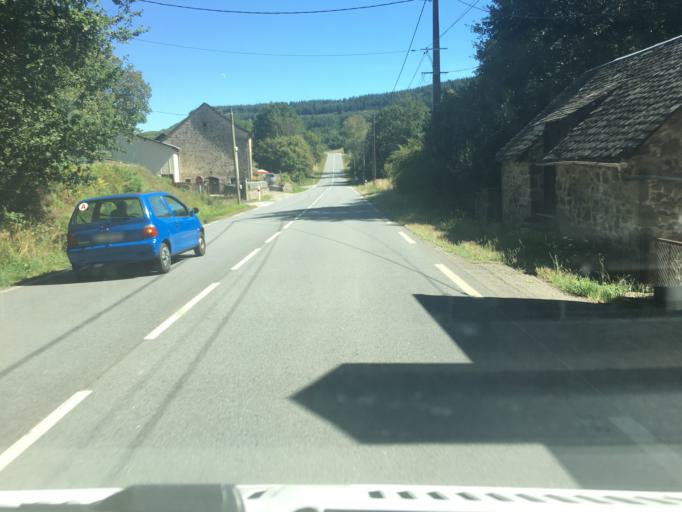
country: FR
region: Limousin
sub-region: Departement de la Correze
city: Bort-les-Orgues
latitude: 45.4183
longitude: 2.4591
